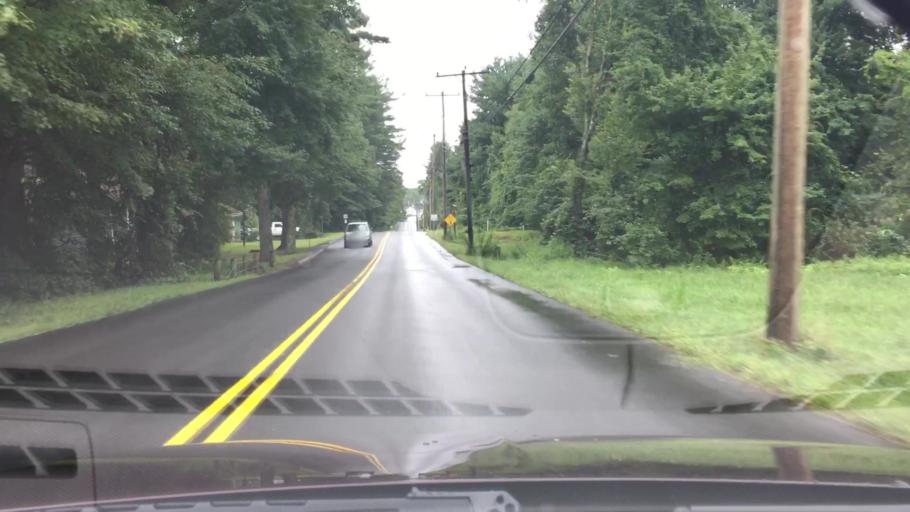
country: US
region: Connecticut
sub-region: Hartford County
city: Tariffville
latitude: 41.9127
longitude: -72.7835
